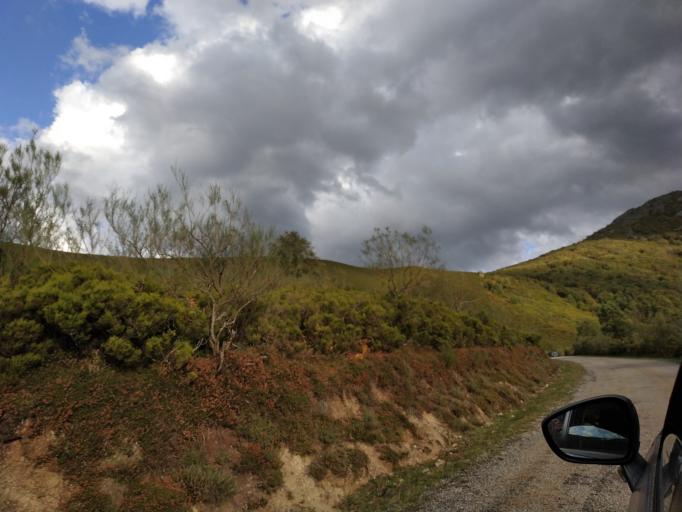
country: ES
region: Castille and Leon
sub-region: Provincia de Leon
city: Candin
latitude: 42.8680
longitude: -6.8369
